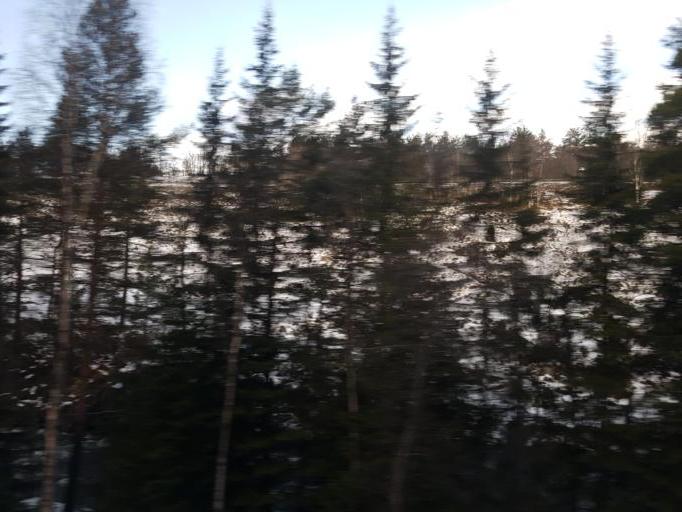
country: NO
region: Sor-Trondelag
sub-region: Rennebu
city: Berkak
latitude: 62.7025
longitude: 9.9482
